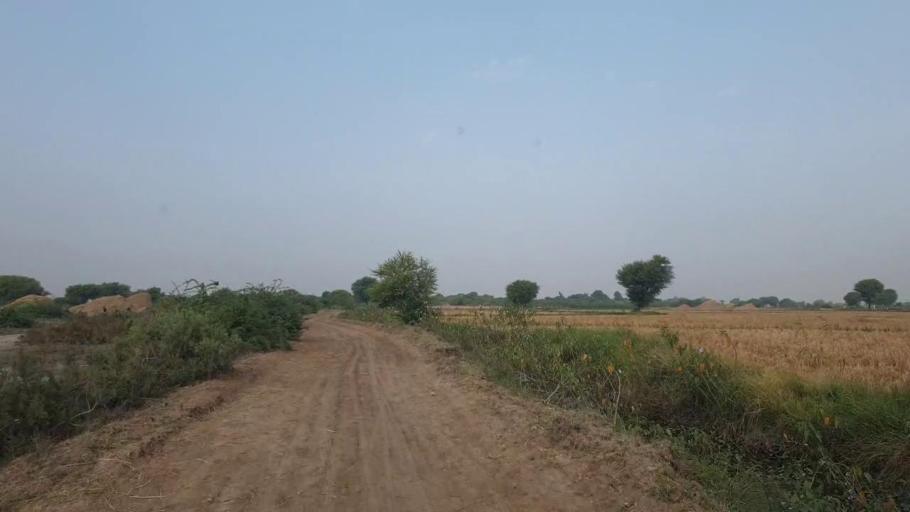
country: PK
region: Sindh
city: Talhar
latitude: 24.8406
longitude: 68.8023
